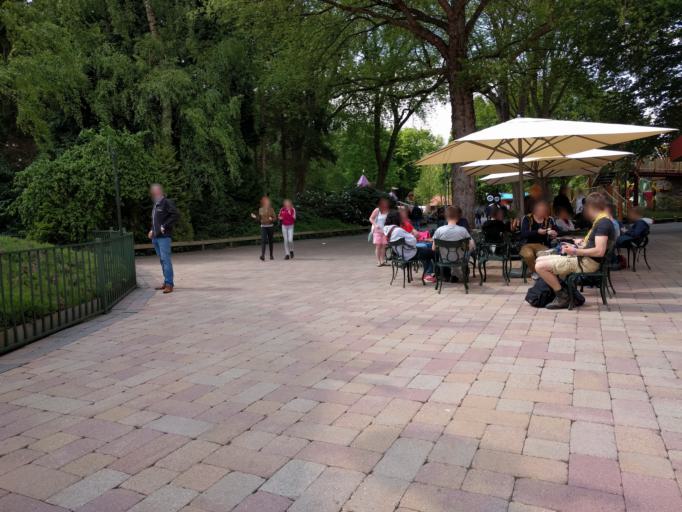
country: NL
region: Gelderland
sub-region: Gemeente Nunspeet
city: Nunspeet
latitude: 52.4407
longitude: 5.7672
